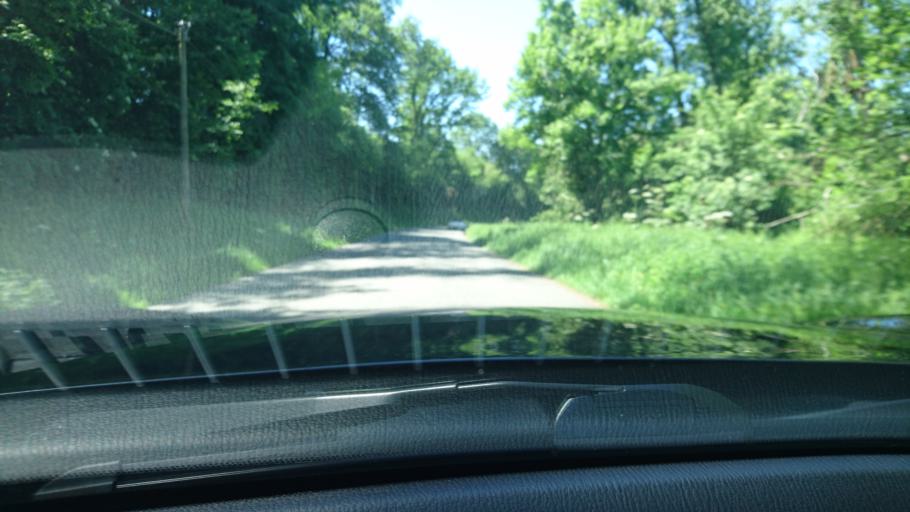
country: FR
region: Rhone-Alpes
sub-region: Departement de la Loire
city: Panissieres
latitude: 45.7899
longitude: 4.3321
